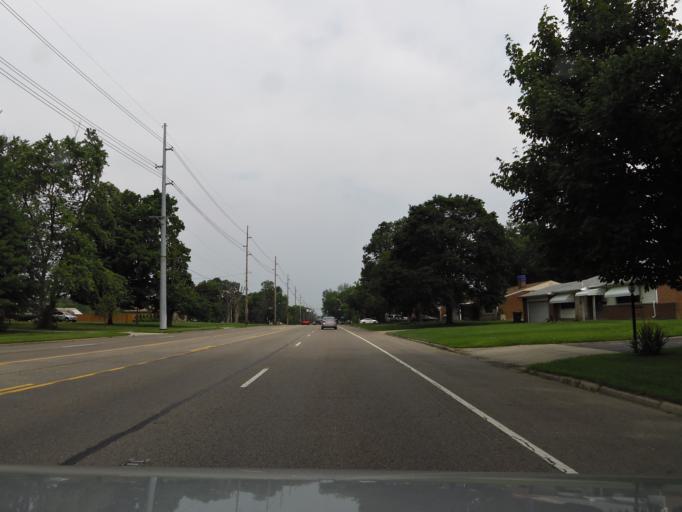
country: US
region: Ohio
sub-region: Greene County
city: Bellbrook
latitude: 39.6697
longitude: -84.1107
